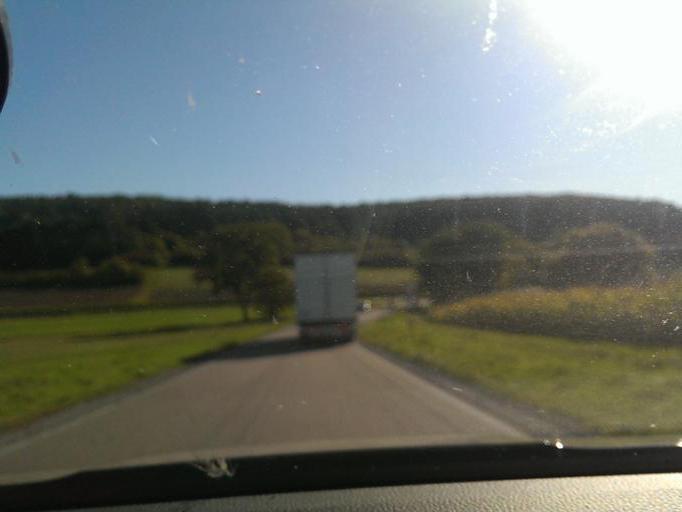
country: DE
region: Baden-Wuerttemberg
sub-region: Karlsruhe Region
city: Friolzheim
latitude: 48.8226
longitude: 8.8310
